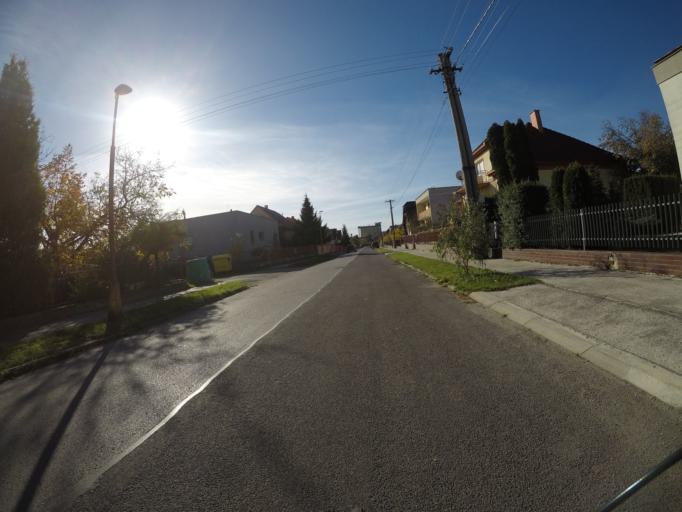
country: SK
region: Trenciansky
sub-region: Okres Nove Mesto nad Vahom
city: Nove Mesto nad Vahom
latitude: 48.7474
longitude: 17.8266
